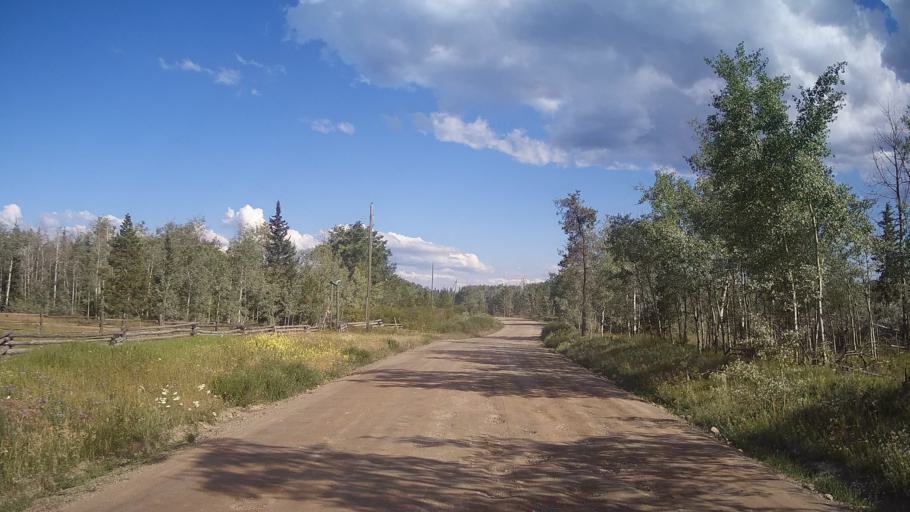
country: CA
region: British Columbia
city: Cache Creek
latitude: 51.2629
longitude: -121.6957
